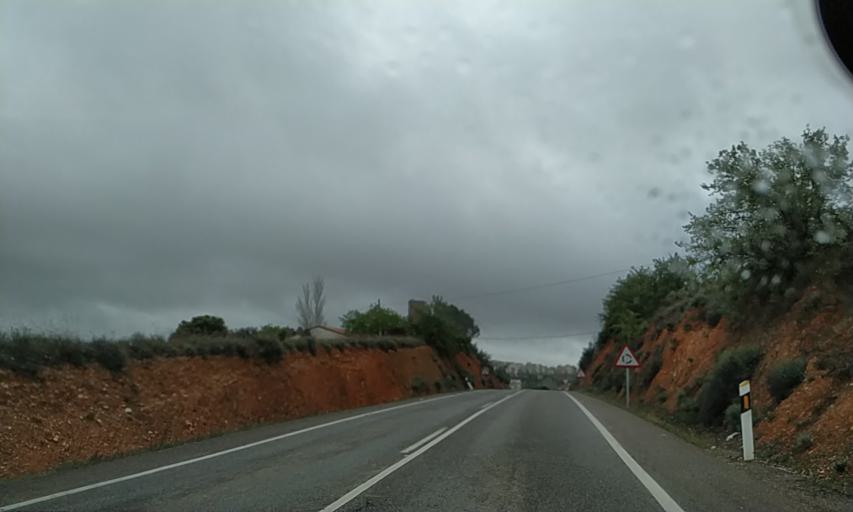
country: ES
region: Extremadura
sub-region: Provincia de Caceres
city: Caceres
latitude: 39.4889
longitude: -6.3835
